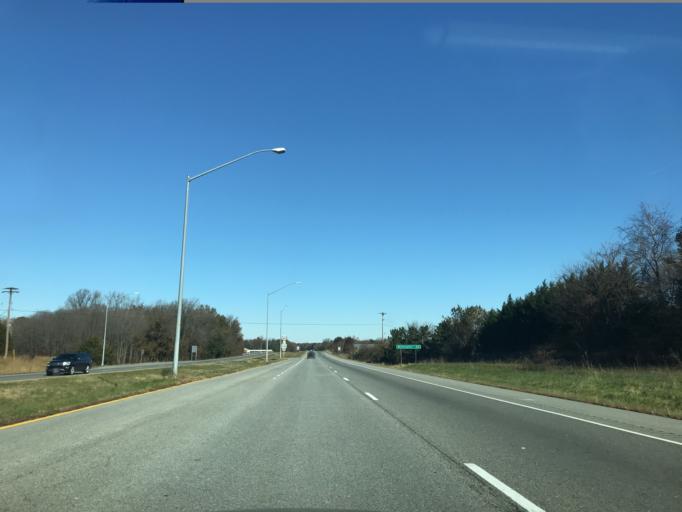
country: US
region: Maryland
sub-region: Queen Anne's County
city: Kingstown
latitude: 39.2436
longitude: -75.8729
